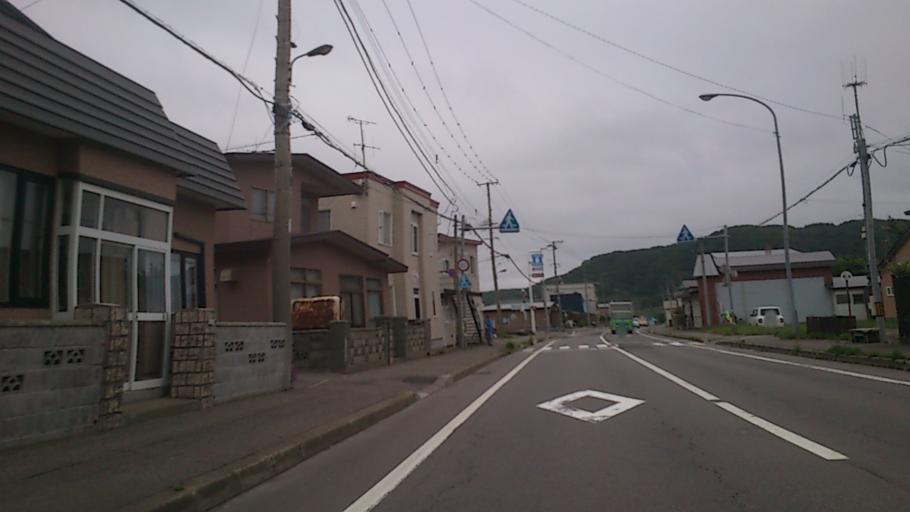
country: JP
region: Hokkaido
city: Kamiiso
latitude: 41.9769
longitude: 140.1346
